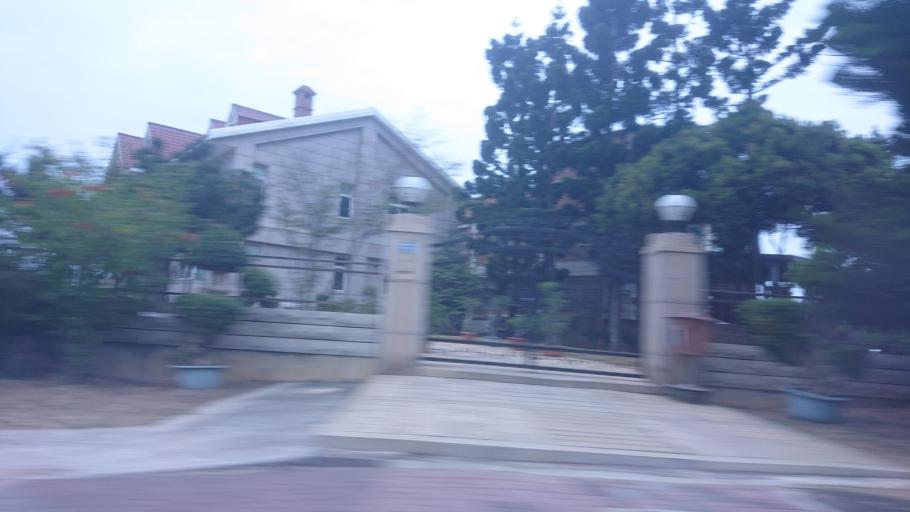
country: TW
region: Fukien
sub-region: Kinmen
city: Jincheng
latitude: 24.4421
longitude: 118.3118
